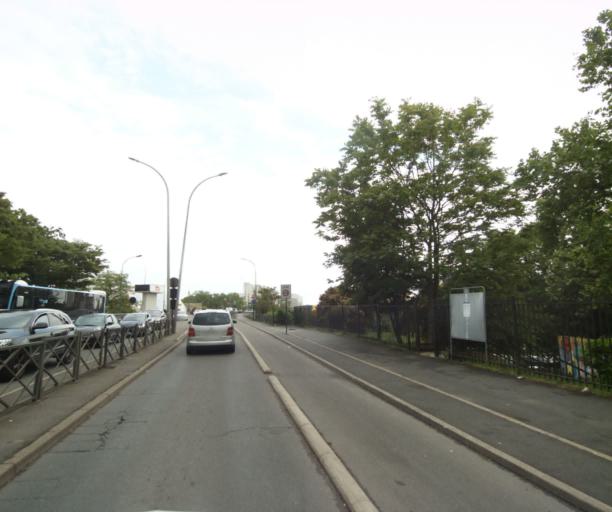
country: FR
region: Ile-de-France
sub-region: Departement du Val-d'Oise
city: Argenteuil
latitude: 48.9511
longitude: 2.2297
